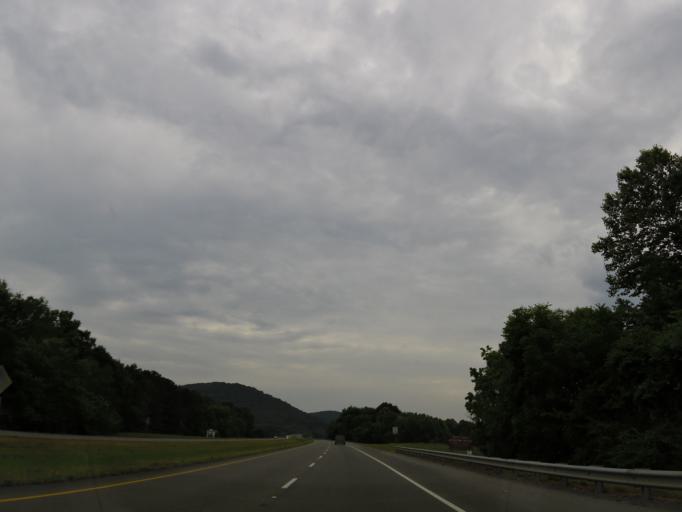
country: US
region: Alabama
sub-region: Jackson County
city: Scottsboro
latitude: 34.6210
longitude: -86.0999
